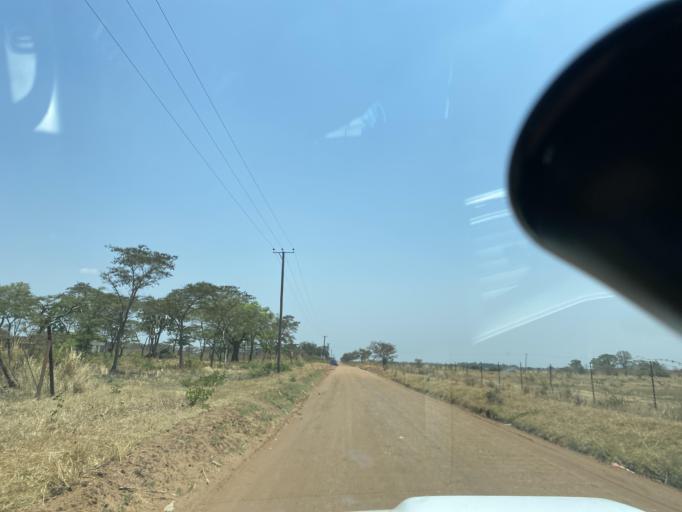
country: ZM
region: Lusaka
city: Lusaka
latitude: -15.4393
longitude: 28.0614
